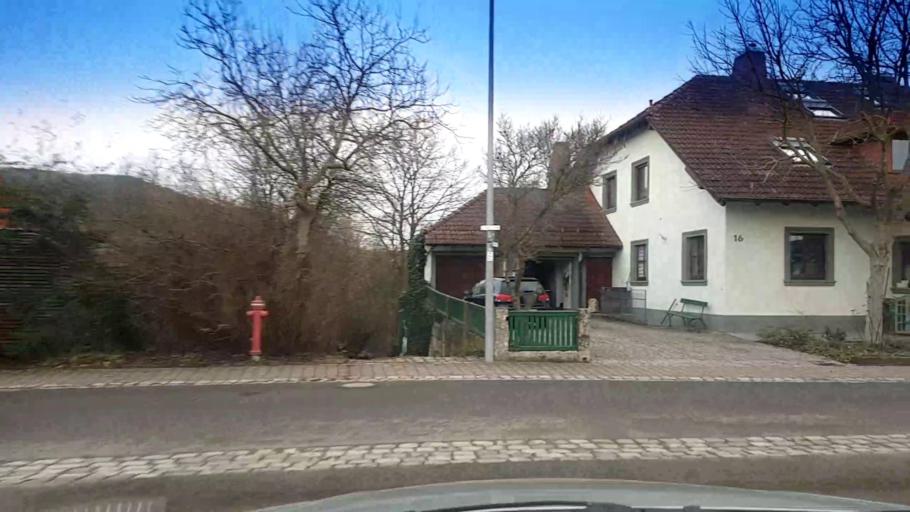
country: DE
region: Bavaria
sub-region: Upper Franconia
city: Schesslitz
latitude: 49.9905
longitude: 11.0443
